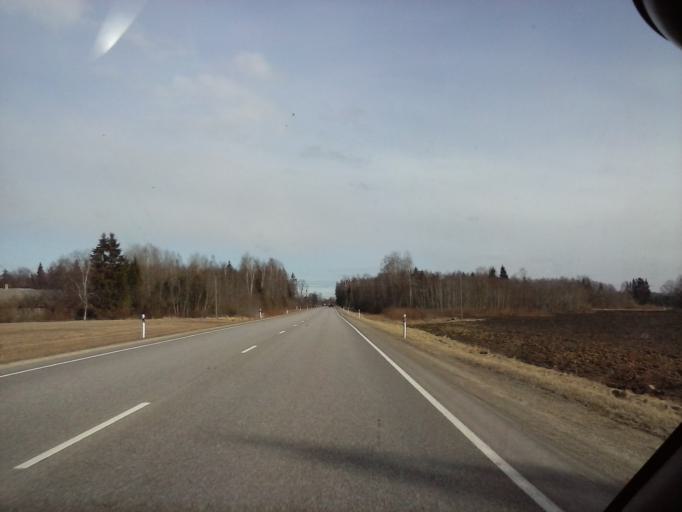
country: EE
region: Jaervamaa
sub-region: Paide linn
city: Paide
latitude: 58.8073
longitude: 25.7578
